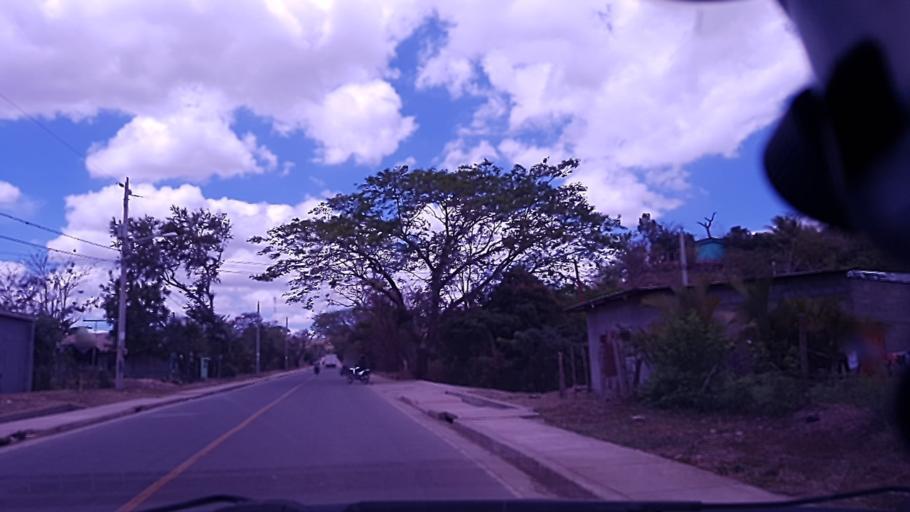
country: NI
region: Esteli
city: Condega
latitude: 13.3750
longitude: -86.3931
